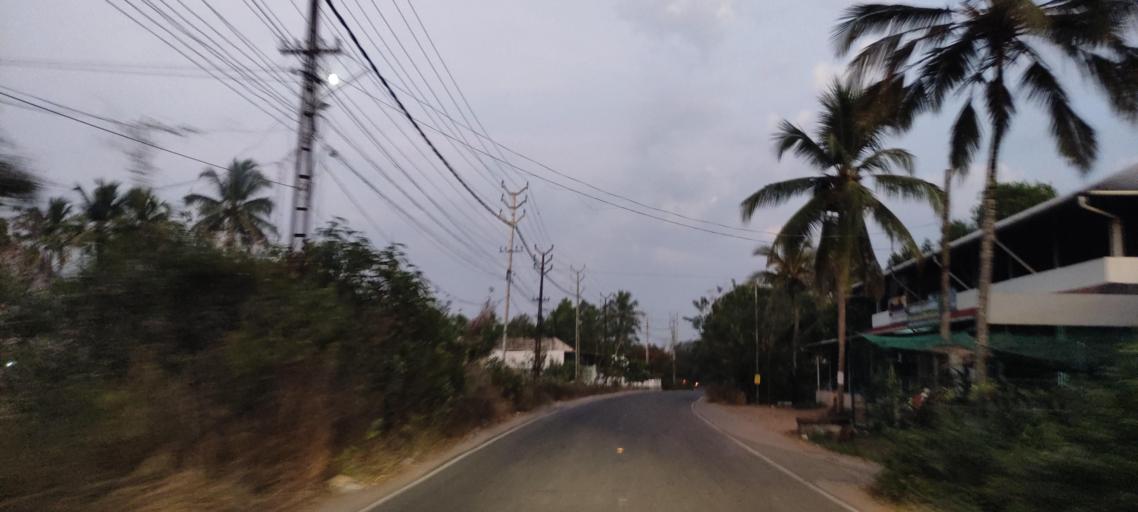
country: IN
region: Kerala
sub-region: Alappuzha
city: Kutiatodu
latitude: 9.7736
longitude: 76.3537
